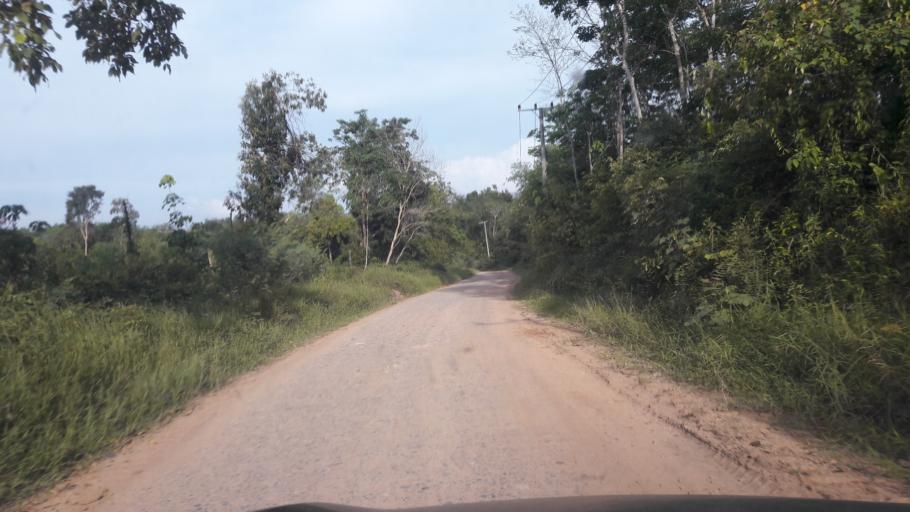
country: ID
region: South Sumatra
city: Gunungmenang
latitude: -3.2624
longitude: 104.0349
